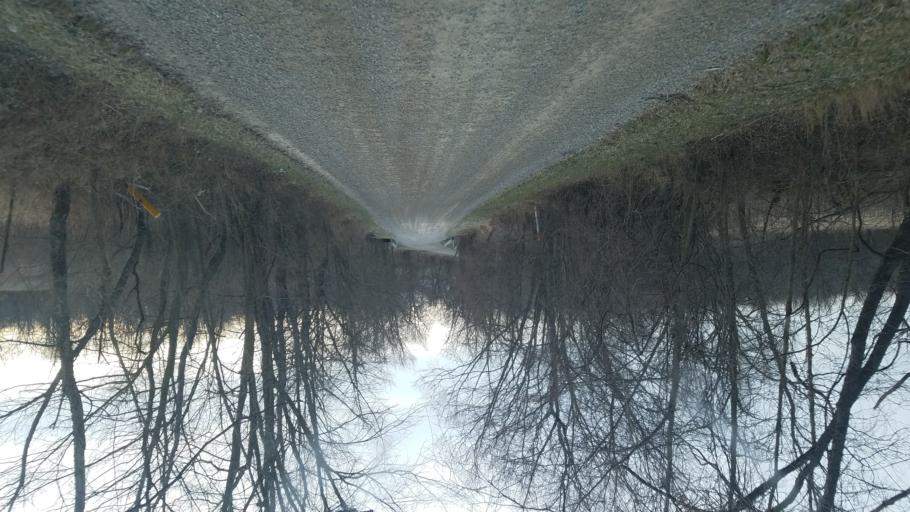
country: US
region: Ohio
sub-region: Morrow County
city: Cardington
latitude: 40.4375
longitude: -82.8023
